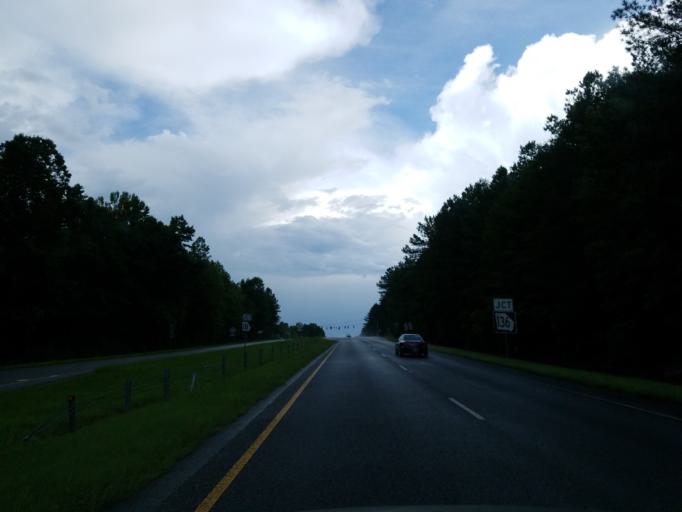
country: US
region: Georgia
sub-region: Dawson County
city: Dawsonville
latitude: 34.3970
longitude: -84.0144
